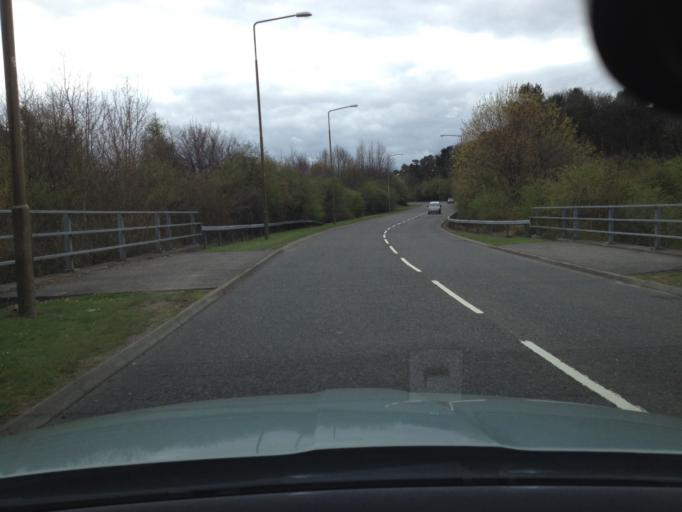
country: GB
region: Scotland
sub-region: West Lothian
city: Livingston
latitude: 55.8921
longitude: -3.5588
